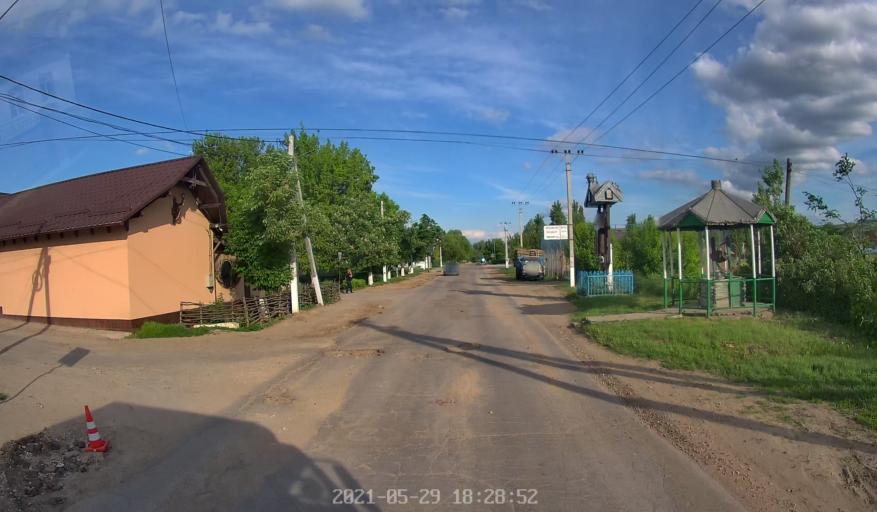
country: MD
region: Chisinau
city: Singera
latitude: 46.8275
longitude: 28.8693
